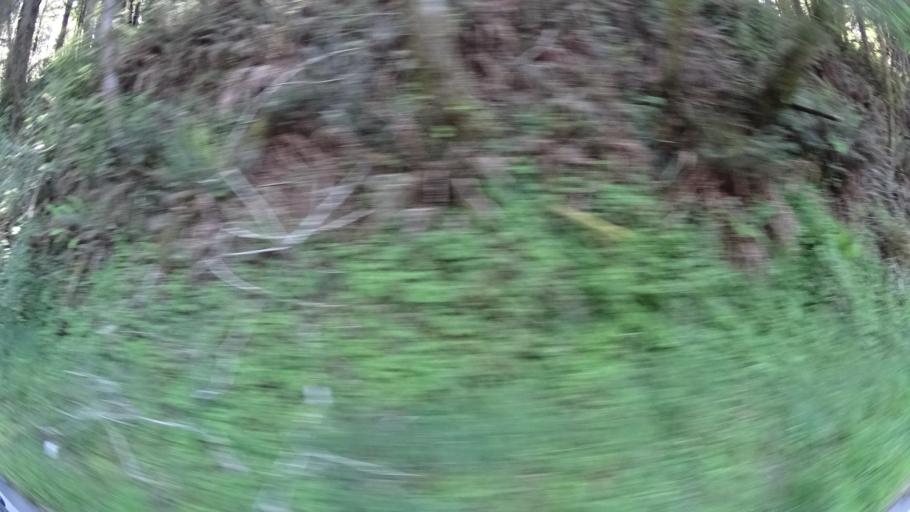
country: US
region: California
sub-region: Humboldt County
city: McKinleyville
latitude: 40.9672
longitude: -124.0676
